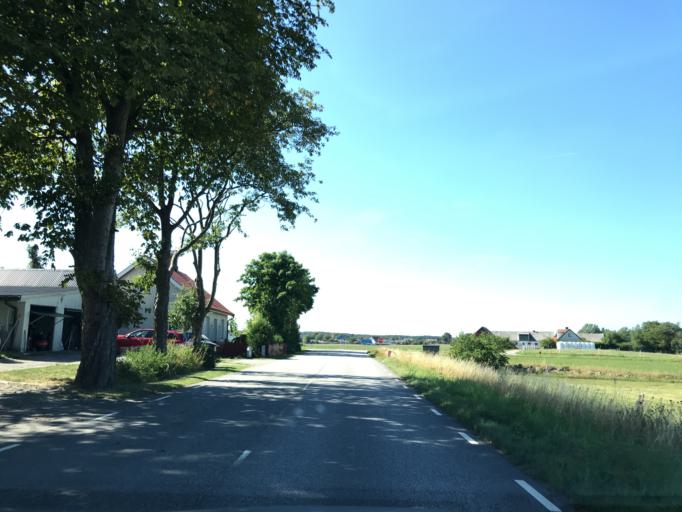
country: SE
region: Skane
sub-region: Tomelilla Kommun
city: Tomelilla
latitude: 55.6552
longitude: 13.9063
